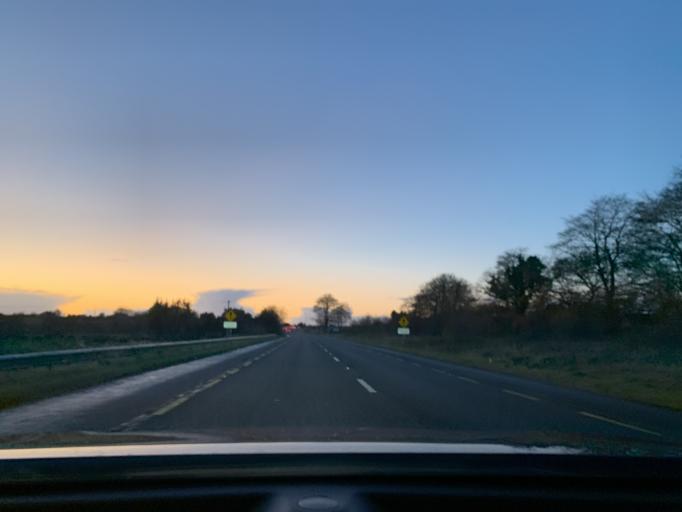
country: IE
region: Connaught
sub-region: County Leitrim
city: Carrick-on-Shannon
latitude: 53.9581
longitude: -8.1722
